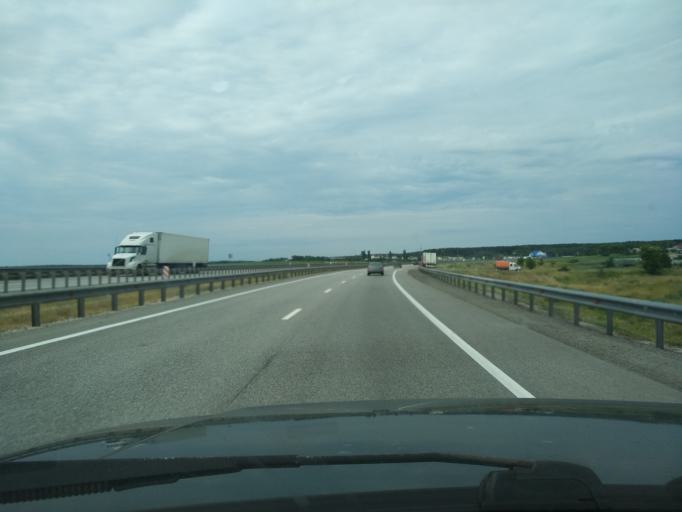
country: RU
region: Lipetsk
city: Khlevnoye
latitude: 52.0674
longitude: 39.1798
